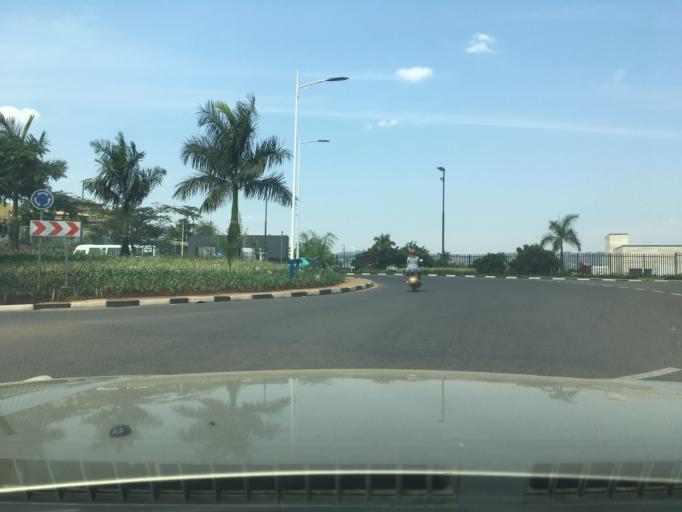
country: RW
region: Kigali
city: Kigali
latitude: -1.9537
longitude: 30.0955
